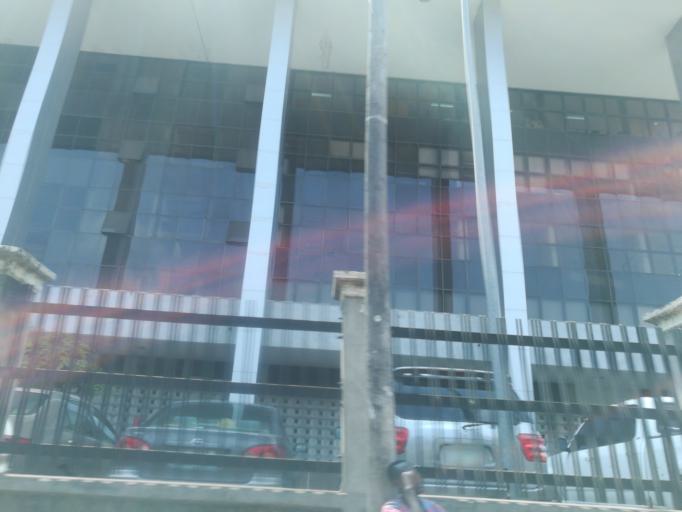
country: NG
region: Lagos
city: Lagos
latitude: 6.4505
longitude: 3.3981
